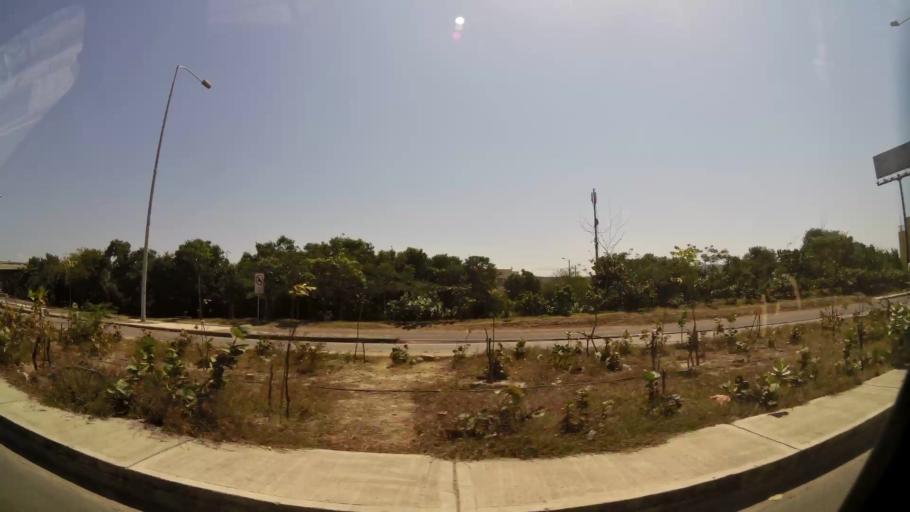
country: CO
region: Bolivar
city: Cartagena
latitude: 10.4419
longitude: -75.5269
